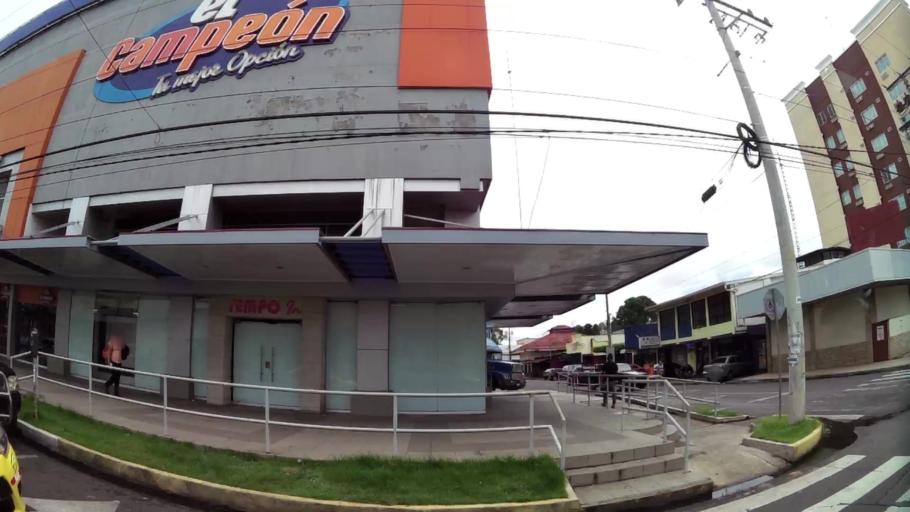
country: PA
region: Chiriqui
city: David
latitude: 8.4266
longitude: -82.4272
